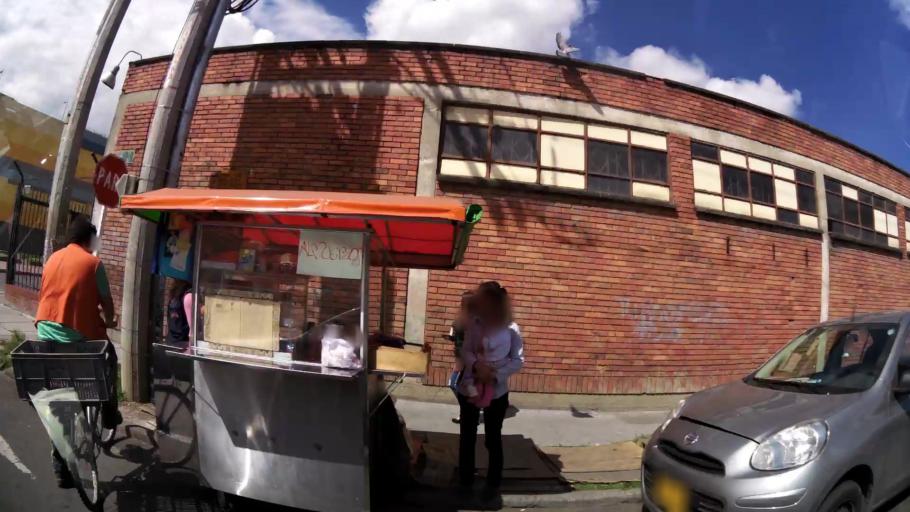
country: CO
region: Bogota D.C.
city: Bogota
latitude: 4.6308
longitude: -74.1151
